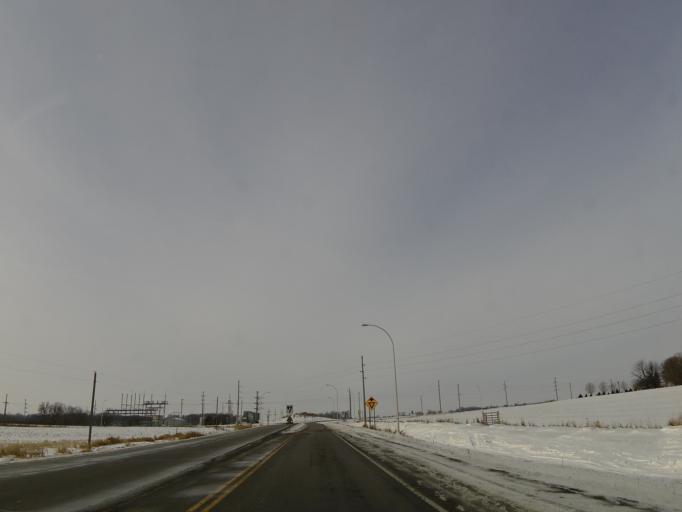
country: US
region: Minnesota
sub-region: Carver County
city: Waconia
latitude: 44.9056
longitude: -93.8156
